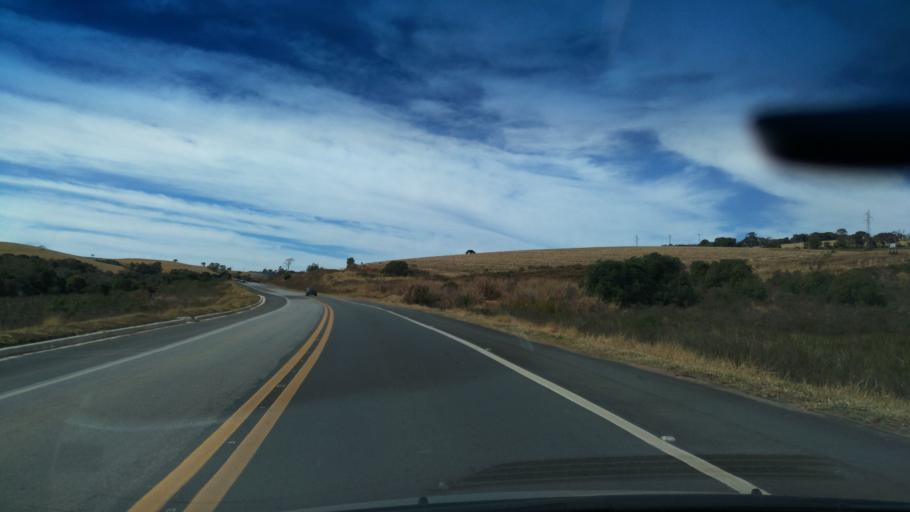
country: BR
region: Minas Gerais
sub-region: Borda Da Mata
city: Borda da Mata
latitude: -22.0639
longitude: -46.2767
